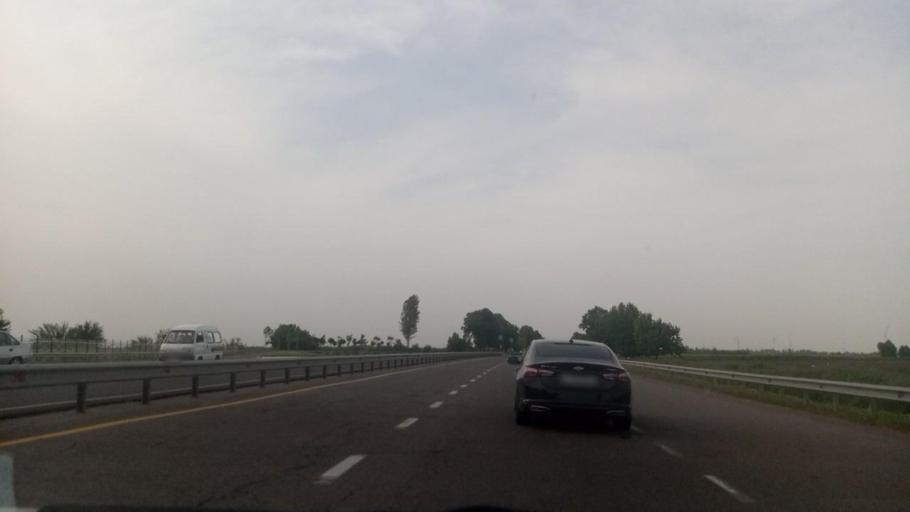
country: UZ
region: Toshkent Shahri
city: Bektemir
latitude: 41.1883
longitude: 69.4036
